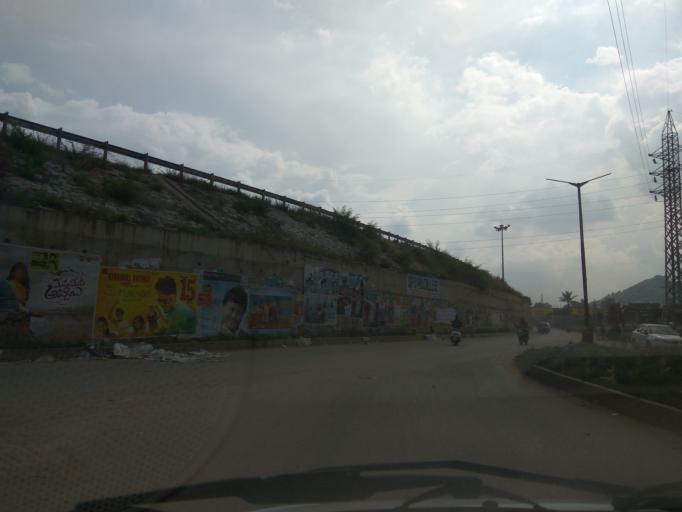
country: IN
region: Karnataka
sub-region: Kolar
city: Kolar
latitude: 13.1265
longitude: 78.1149
